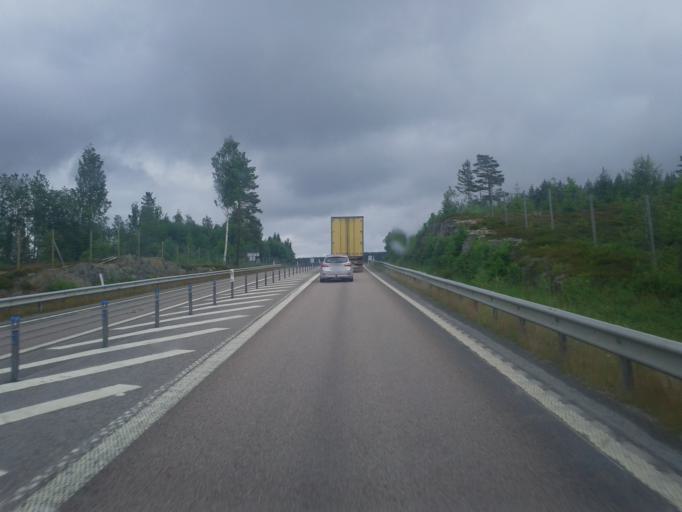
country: SE
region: Vaesternorrland
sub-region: Haernoesands Kommun
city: Haernoesand
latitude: 62.6008
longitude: 17.8124
